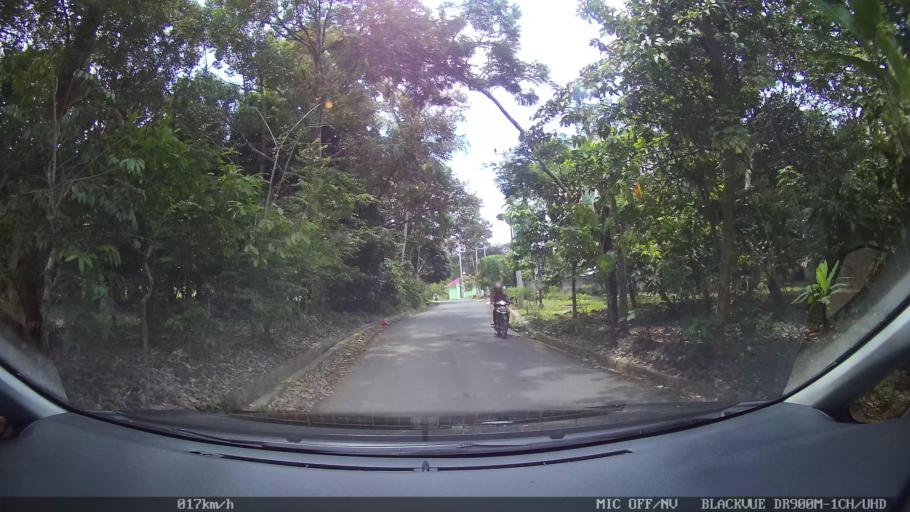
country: ID
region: Lampung
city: Bandarlampung
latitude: -5.4207
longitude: 105.2229
